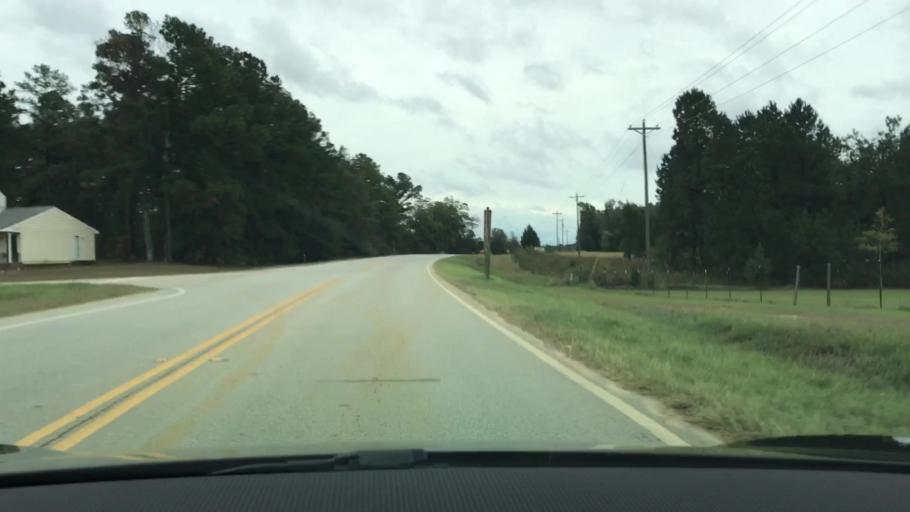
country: US
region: Georgia
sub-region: Jefferson County
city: Wrens
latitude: 33.1884
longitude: -82.4561
